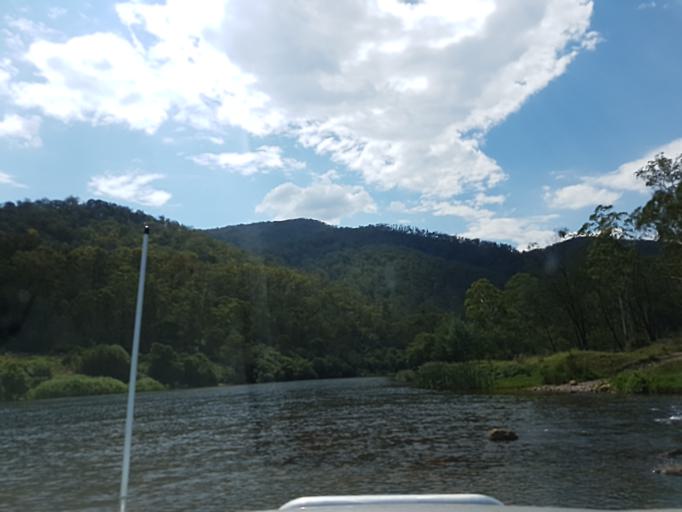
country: AU
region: Victoria
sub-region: East Gippsland
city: Lakes Entrance
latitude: -37.3941
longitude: 148.3337
